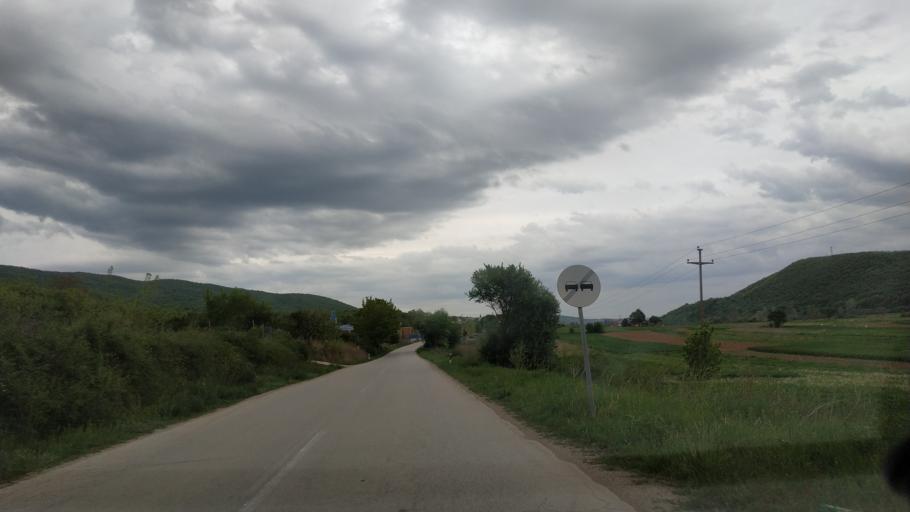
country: RS
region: Central Serbia
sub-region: Nisavski Okrug
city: Aleksinac
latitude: 43.5984
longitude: 21.6880
